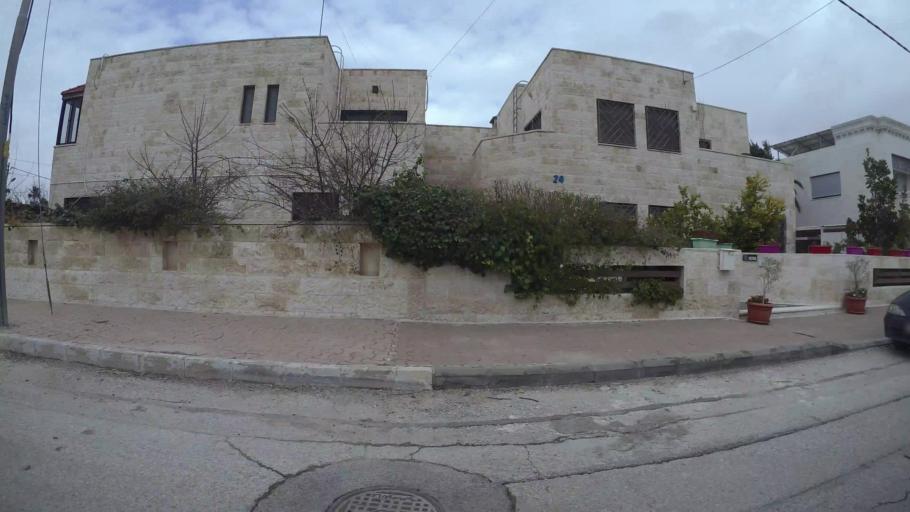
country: JO
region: Amman
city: Wadi as Sir
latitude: 31.9866
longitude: 35.8332
